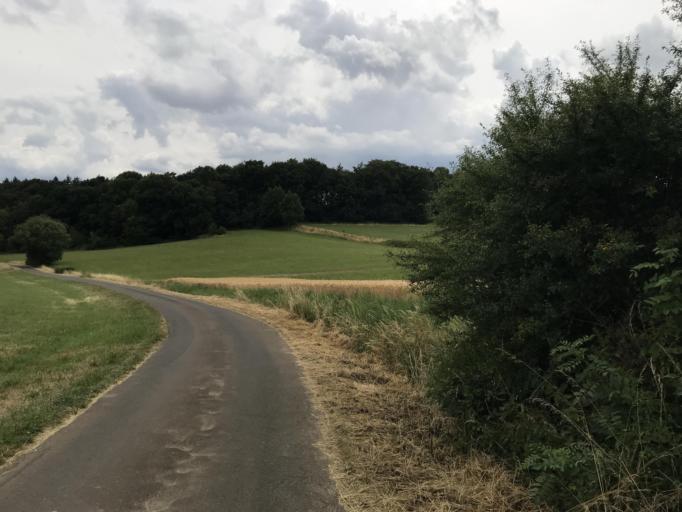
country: DE
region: Hesse
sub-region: Regierungsbezirk Giessen
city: Grunberg
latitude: 50.5901
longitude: 8.9358
